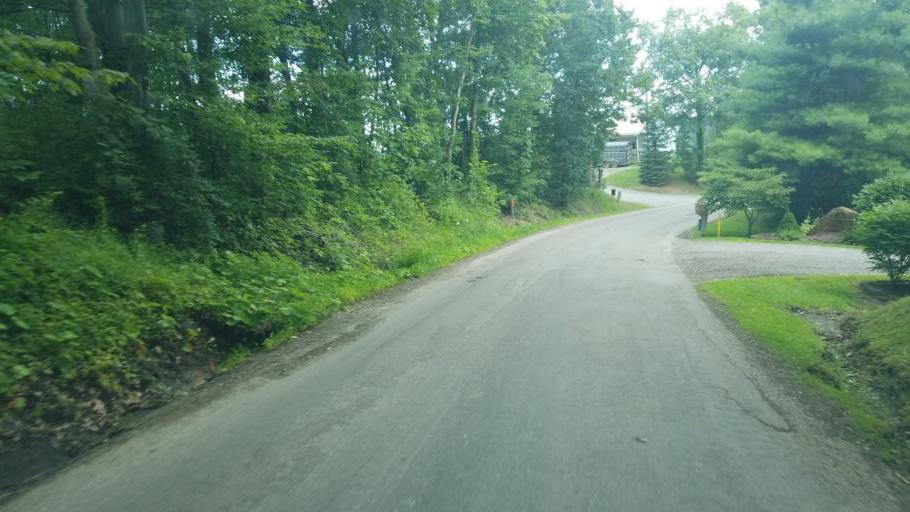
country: US
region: Ohio
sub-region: Holmes County
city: Millersburg
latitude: 40.5108
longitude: -81.8033
